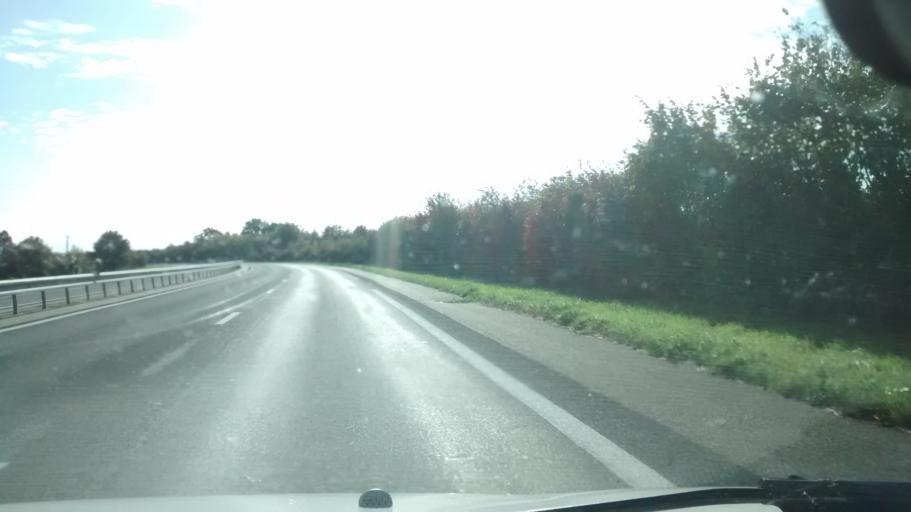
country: FR
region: Pays de la Loire
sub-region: Departement de Maine-et-Loire
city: Pouance
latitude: 47.7416
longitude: -1.1532
